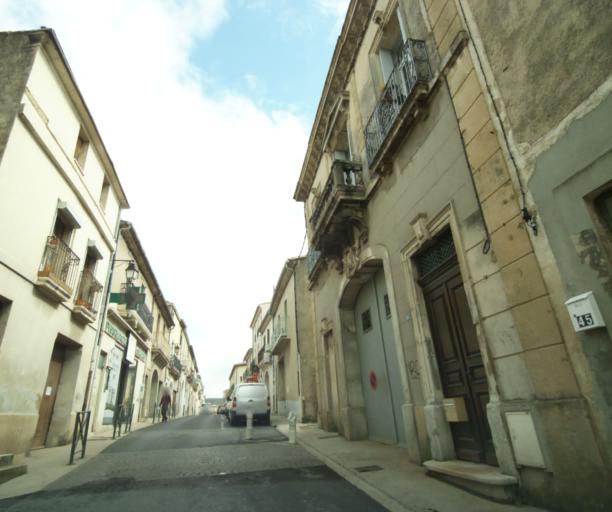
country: FR
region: Languedoc-Roussillon
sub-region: Departement de l'Herault
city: Fabregues
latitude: 43.5507
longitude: 3.7767
